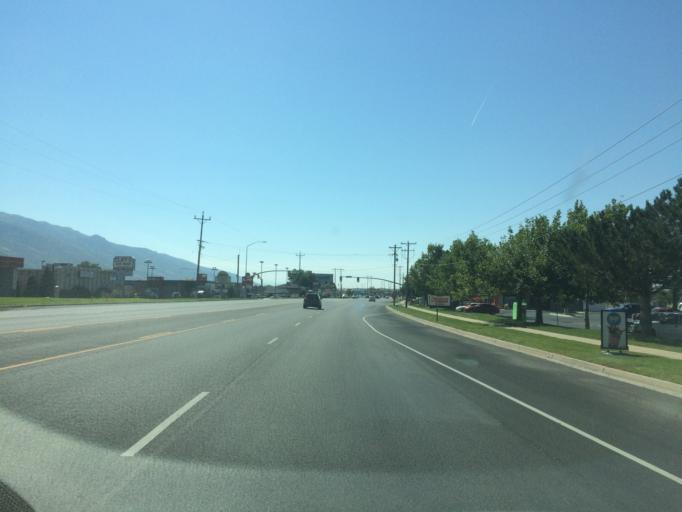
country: US
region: Utah
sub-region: Weber County
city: Uintah
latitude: 41.1604
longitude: -111.9400
